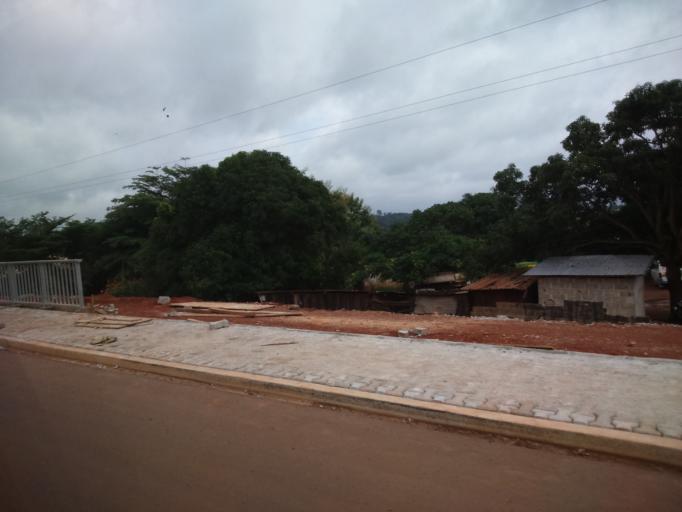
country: CI
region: Moyen-Comoe
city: Abengourou
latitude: 6.7203
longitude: -3.5144
